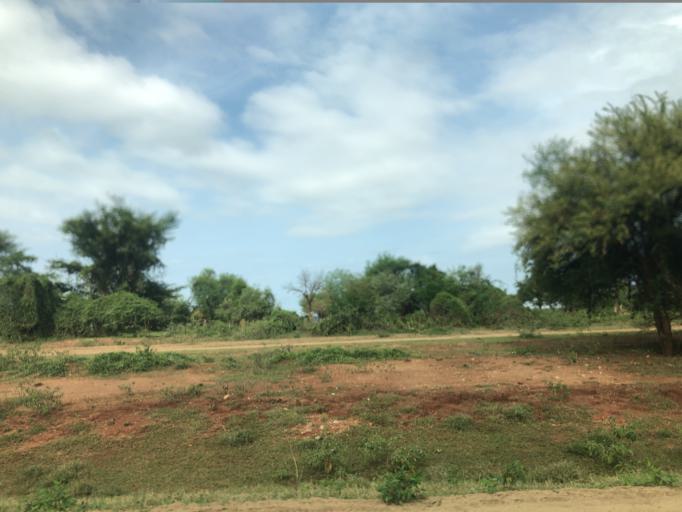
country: ET
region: Southern Nations, Nationalities, and People's Region
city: Turmi
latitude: 5.1343
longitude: 36.5159
